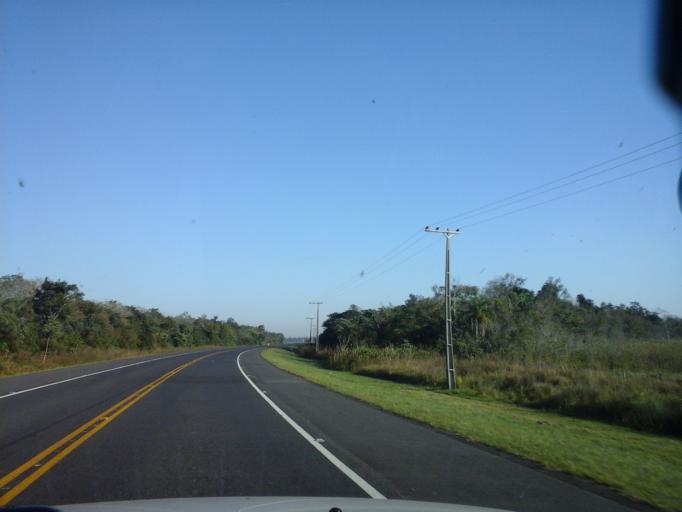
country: PY
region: Neembucu
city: Pilar
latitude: -26.8591
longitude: -57.9559
